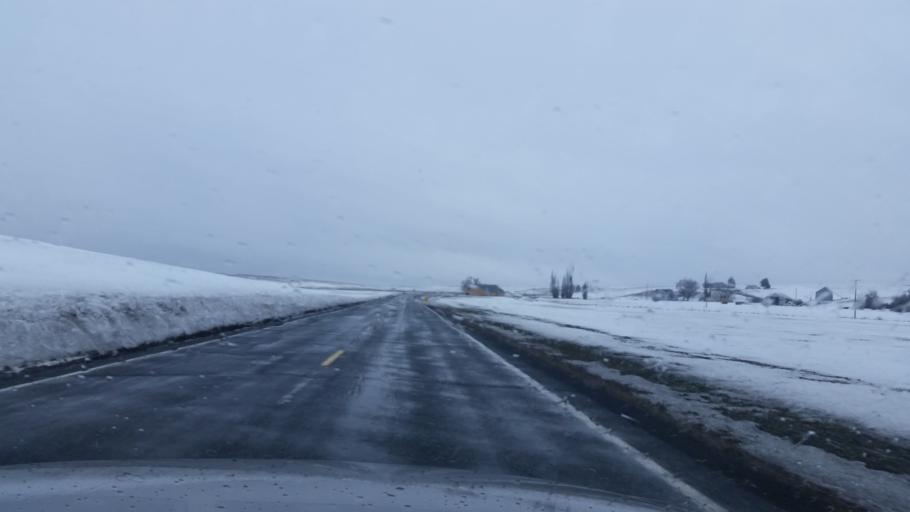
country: US
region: Washington
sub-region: Lincoln County
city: Davenport
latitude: 47.4173
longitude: -118.1797
